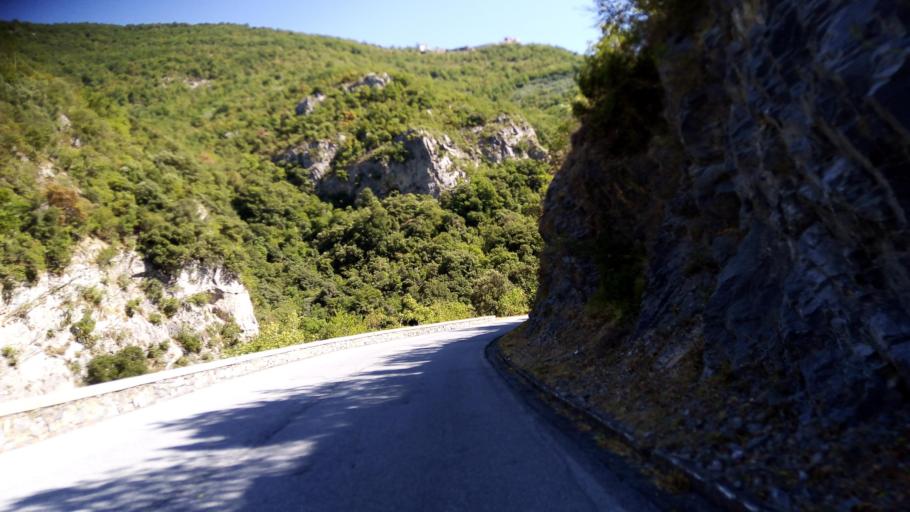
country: IT
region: Liguria
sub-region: Provincia di Savona
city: Balestrino
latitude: 44.1390
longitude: 8.1681
